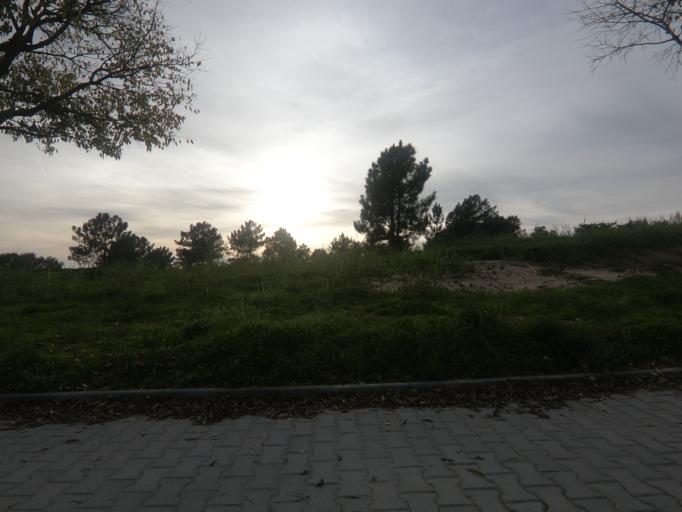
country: PT
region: Setubal
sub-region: Setubal
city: Setubal
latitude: 38.5172
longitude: -8.8653
